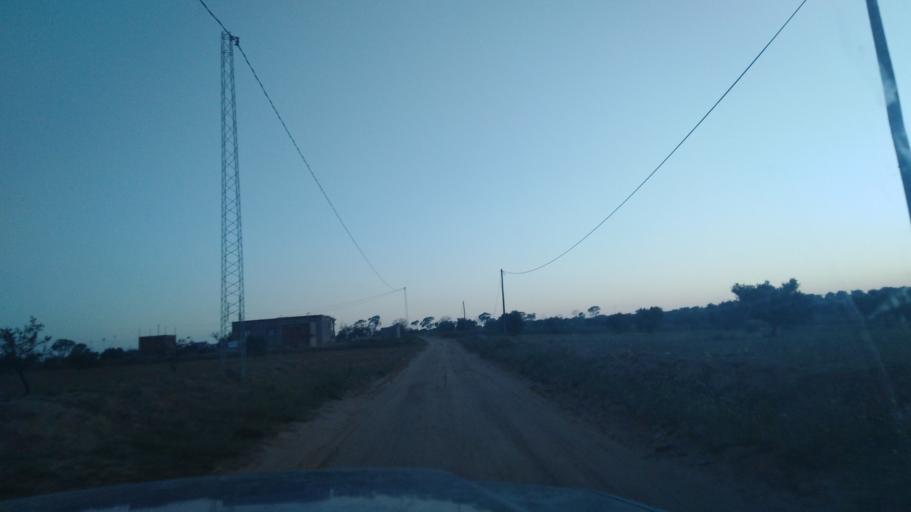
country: TN
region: Safaqis
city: Sfax
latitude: 34.7314
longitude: 10.4871
